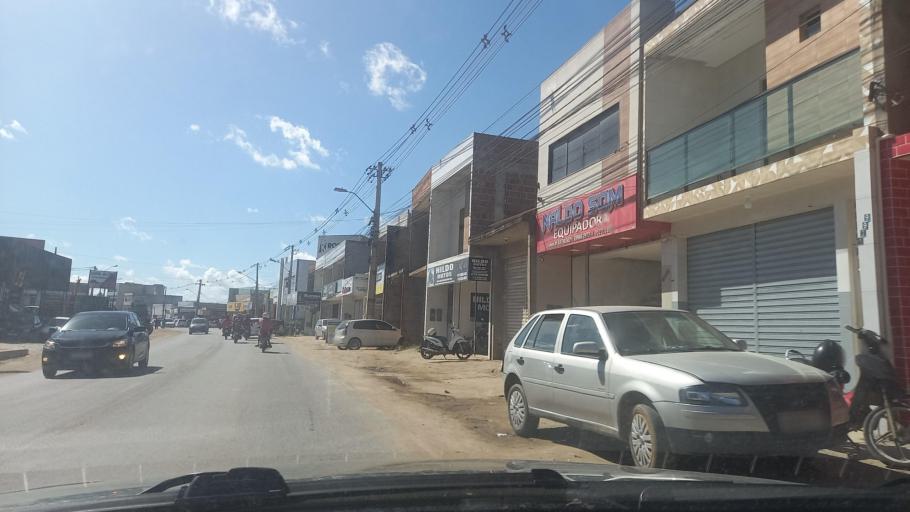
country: BR
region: Pernambuco
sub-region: Vitoria De Santo Antao
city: Vitoria de Santo Antao
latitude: -8.1179
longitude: -35.3000
